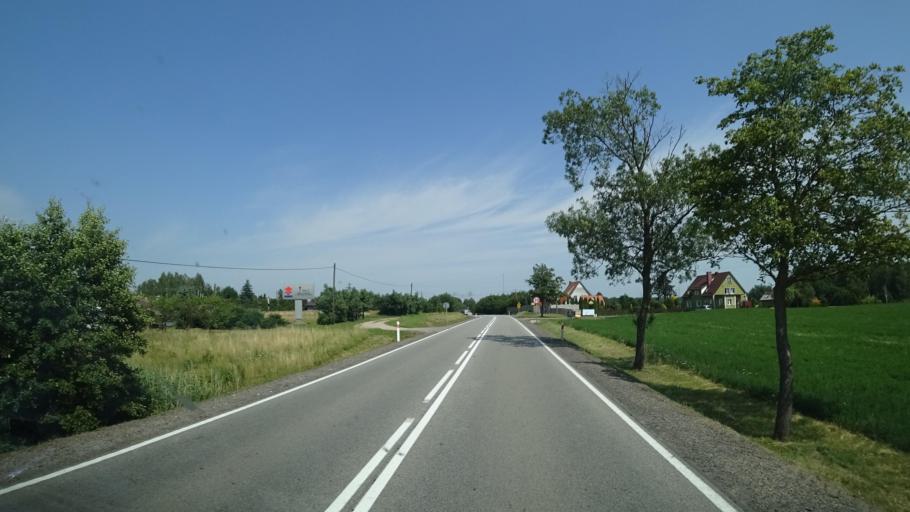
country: PL
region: Pomeranian Voivodeship
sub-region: Powiat koscierski
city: Koscierzyna
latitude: 54.1433
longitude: 18.0228
